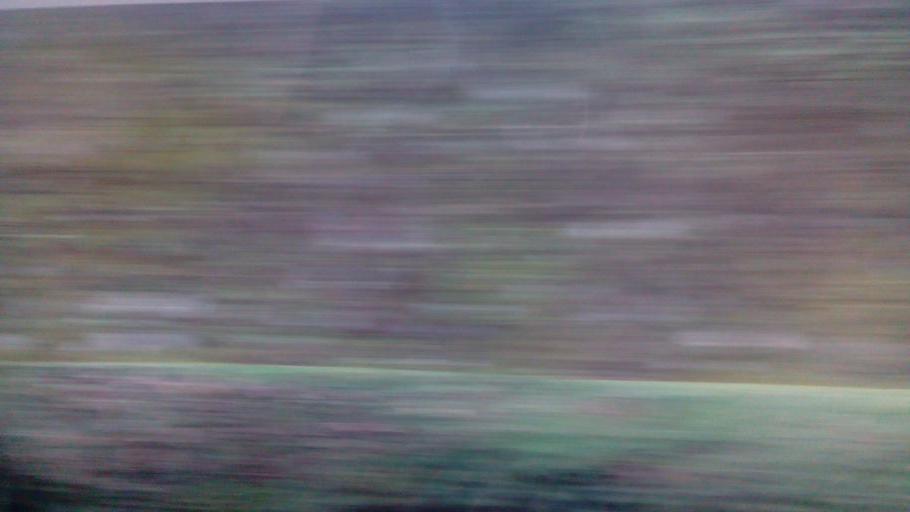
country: TW
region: Taiwan
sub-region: Yilan
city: Yilan
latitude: 24.5760
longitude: 121.4826
